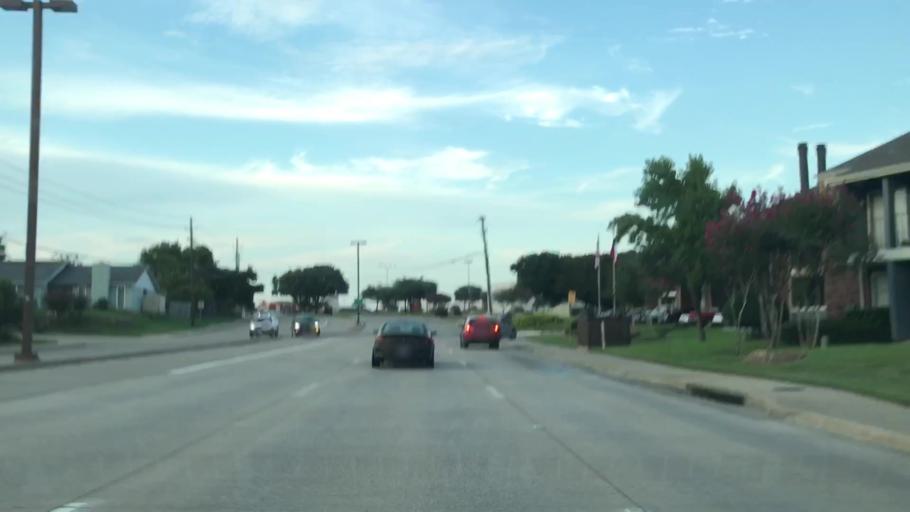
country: US
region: Texas
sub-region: Dallas County
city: Carrollton
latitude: 32.9961
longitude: -96.8877
